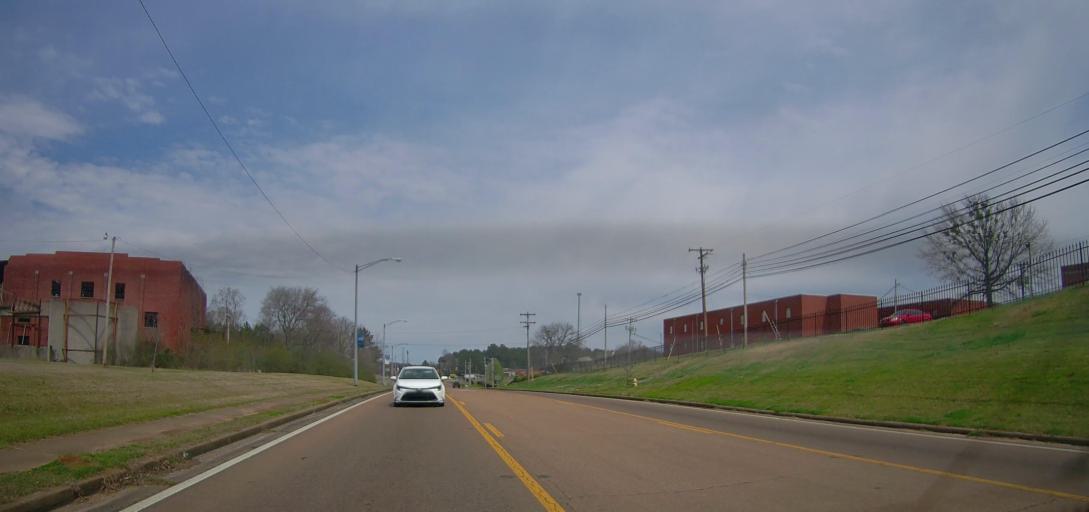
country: US
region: Mississippi
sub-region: Marshall County
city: Holly Springs
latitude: 34.7763
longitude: -89.4486
